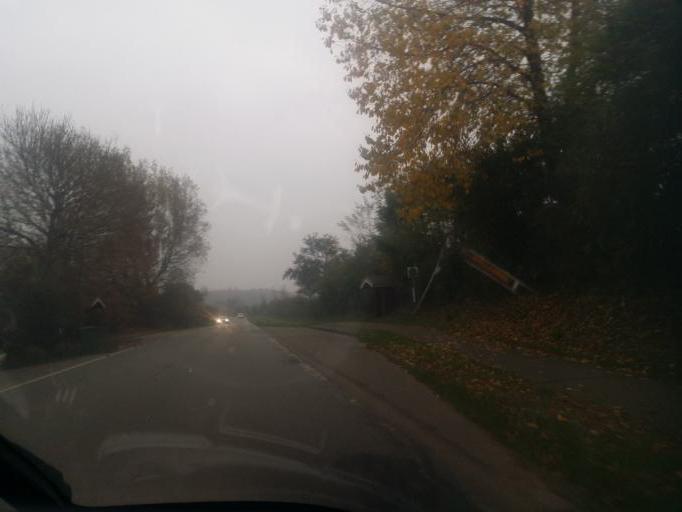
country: DE
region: Schleswig-Holstein
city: Grosssolt
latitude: 54.7019
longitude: 9.5397
